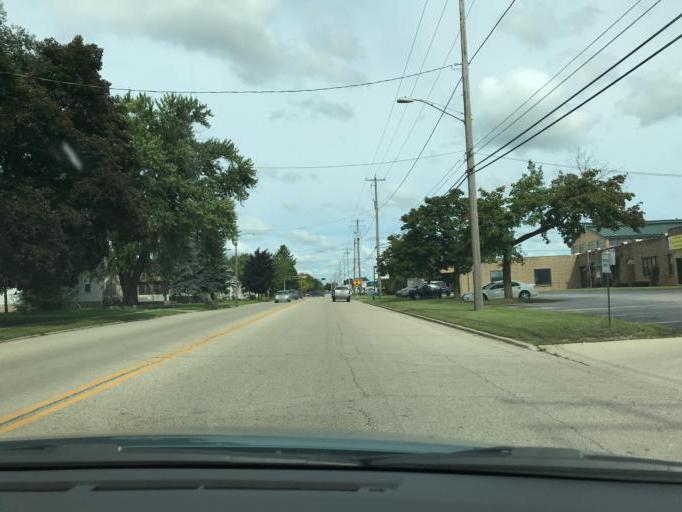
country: US
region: Wisconsin
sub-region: Racine County
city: Burlington
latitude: 42.6701
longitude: -88.2686
